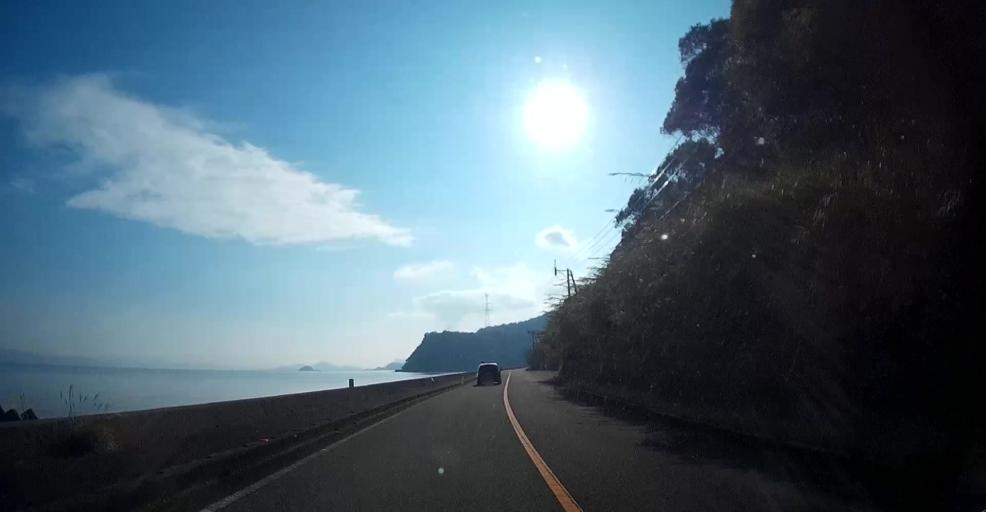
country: JP
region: Kumamoto
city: Yatsushiro
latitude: 32.5150
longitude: 130.4560
